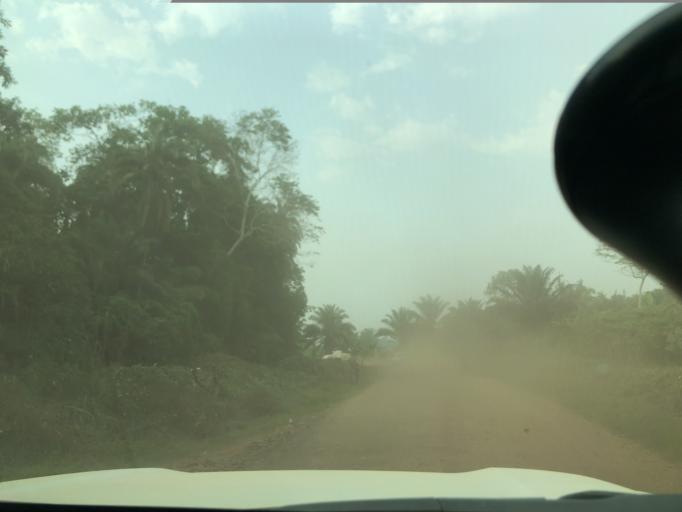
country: UG
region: Western Region
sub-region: Kasese District
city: Margherita
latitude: 0.2815
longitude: 29.6697
